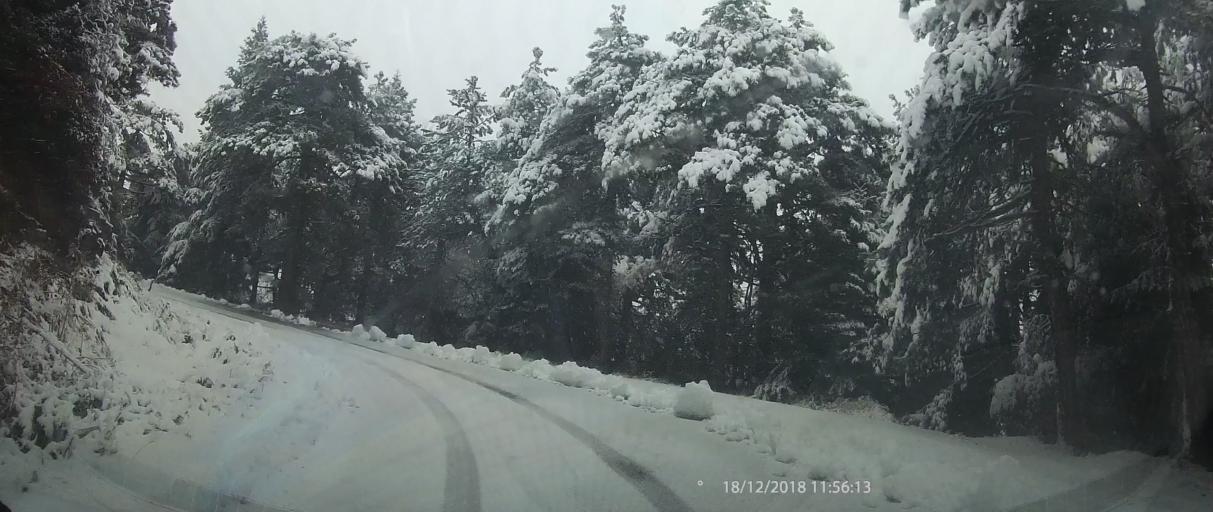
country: GR
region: Central Macedonia
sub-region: Nomos Pierias
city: Litochoro
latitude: 40.1119
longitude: 22.4714
